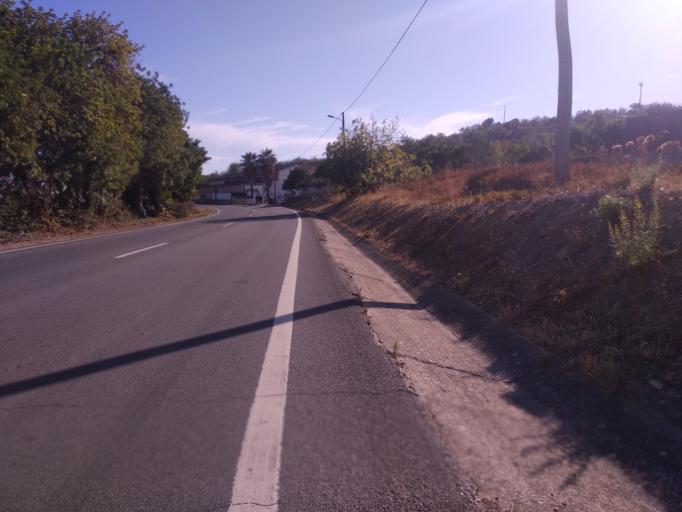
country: PT
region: Faro
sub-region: Sao Bras de Alportel
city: Sao Bras de Alportel
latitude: 37.1139
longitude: -7.9079
